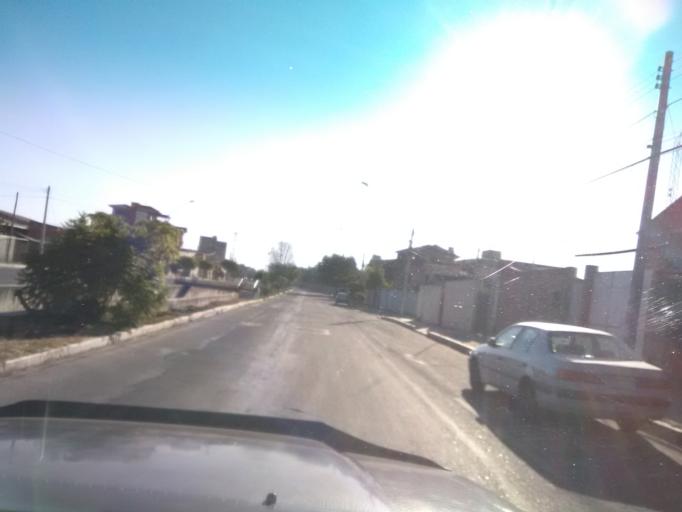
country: BO
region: Cochabamba
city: Cochabamba
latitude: -17.3824
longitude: -66.1905
